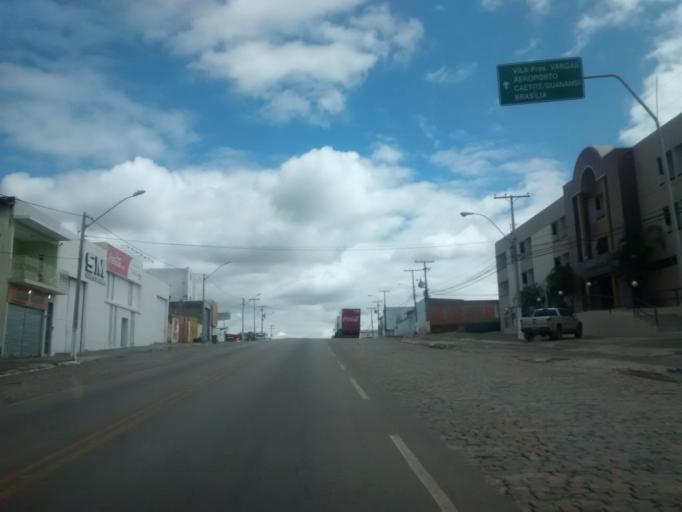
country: BR
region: Bahia
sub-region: Brumado
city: Brumado
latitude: -14.2163
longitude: -41.6821
